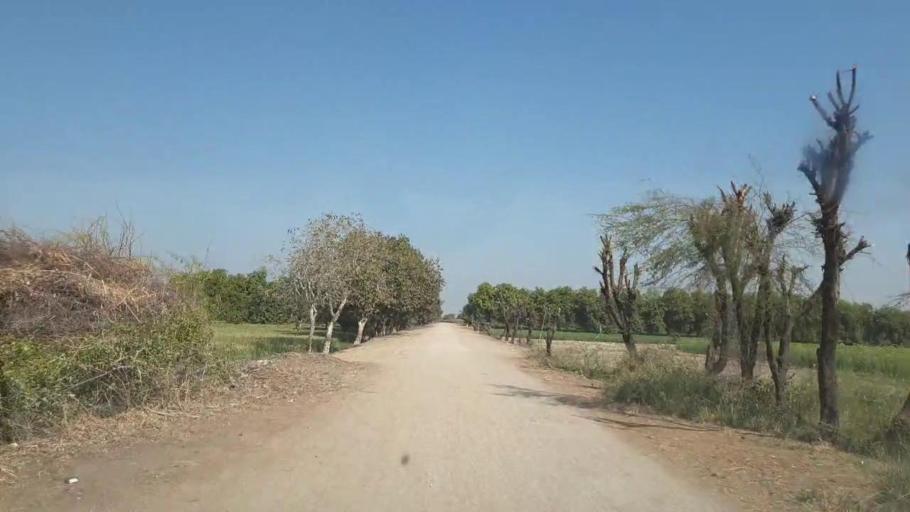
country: PK
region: Sindh
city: Mirpur Khas
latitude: 25.6666
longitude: 69.1106
